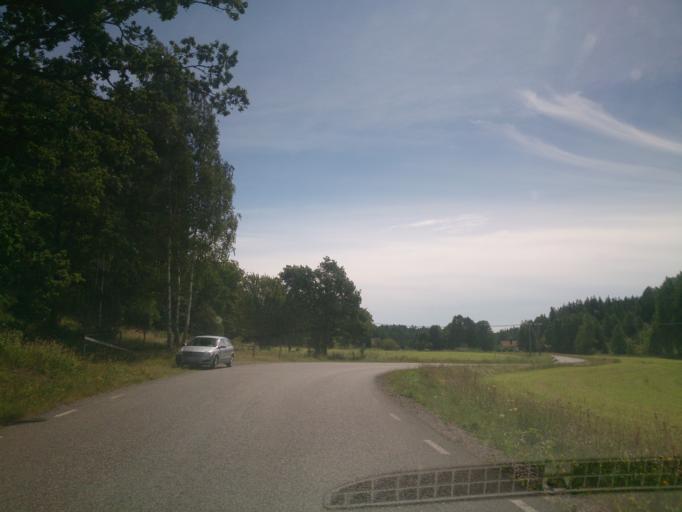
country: SE
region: OEstergoetland
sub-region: Valdemarsviks Kommun
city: Valdemarsvik
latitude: 58.2801
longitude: 16.6897
